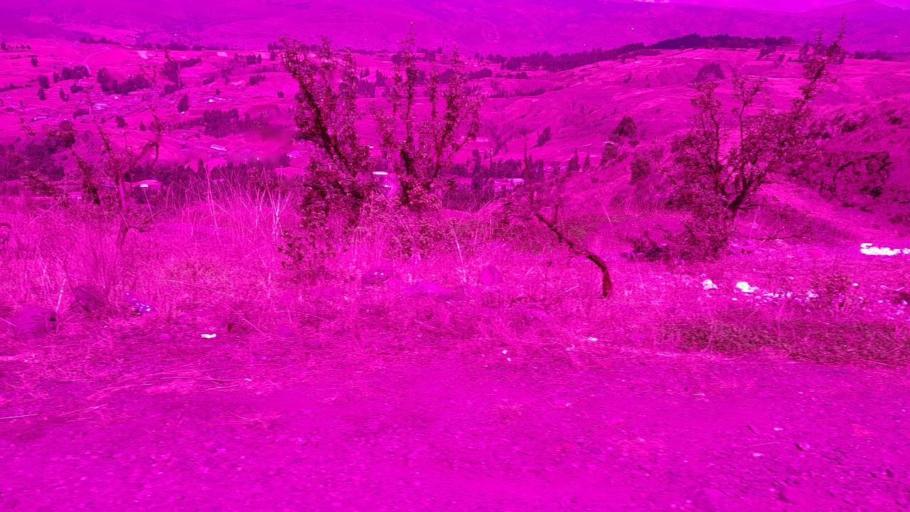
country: PE
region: Cusco
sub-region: Provincia de Cusco
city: Cusco
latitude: -13.4925
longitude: -71.9298
